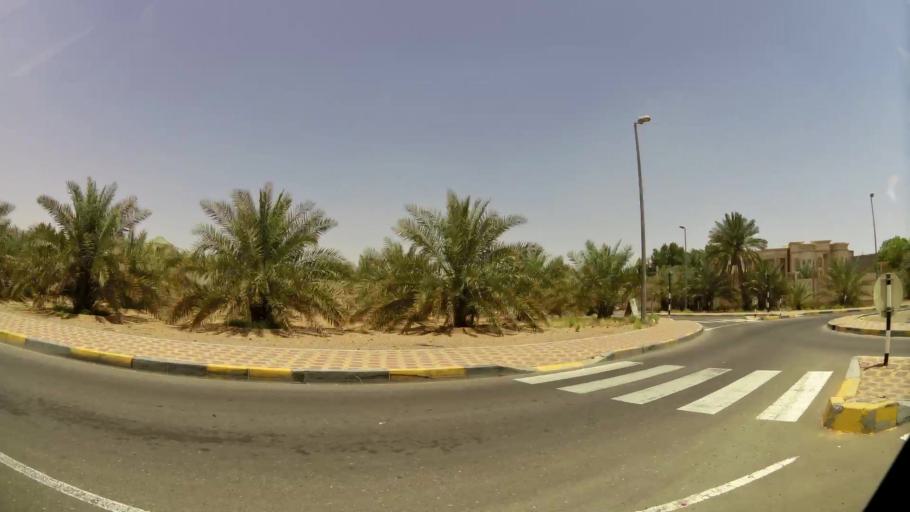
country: OM
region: Al Buraimi
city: Al Buraymi
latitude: 24.2685
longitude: 55.7063
